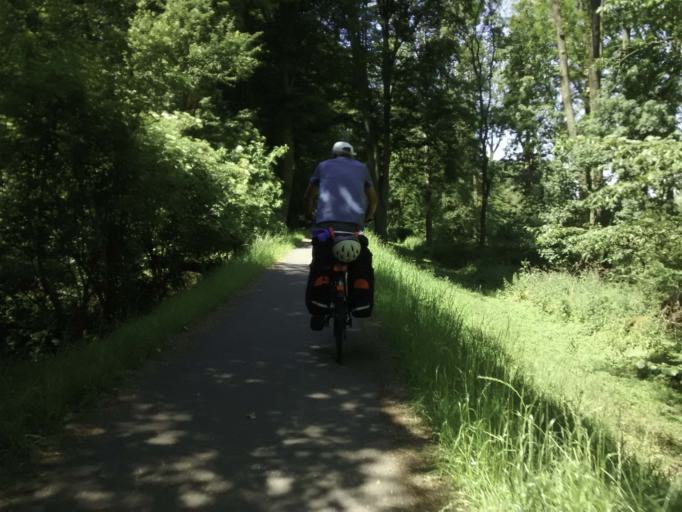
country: DE
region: Saxony-Anhalt
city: Vockerode
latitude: 51.8638
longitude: 12.3297
